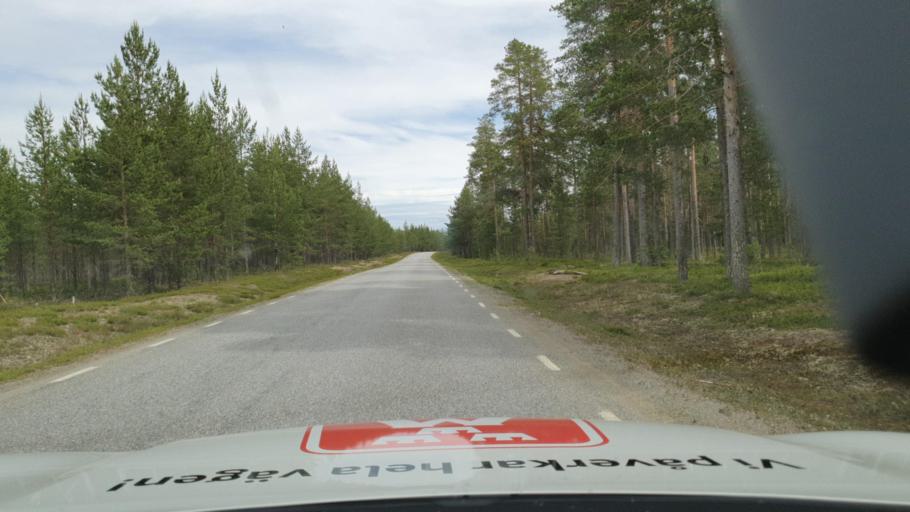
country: SE
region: Vaesterbotten
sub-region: Skelleftea Kommun
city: Burtraesk
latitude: 64.5054
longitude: 20.7883
